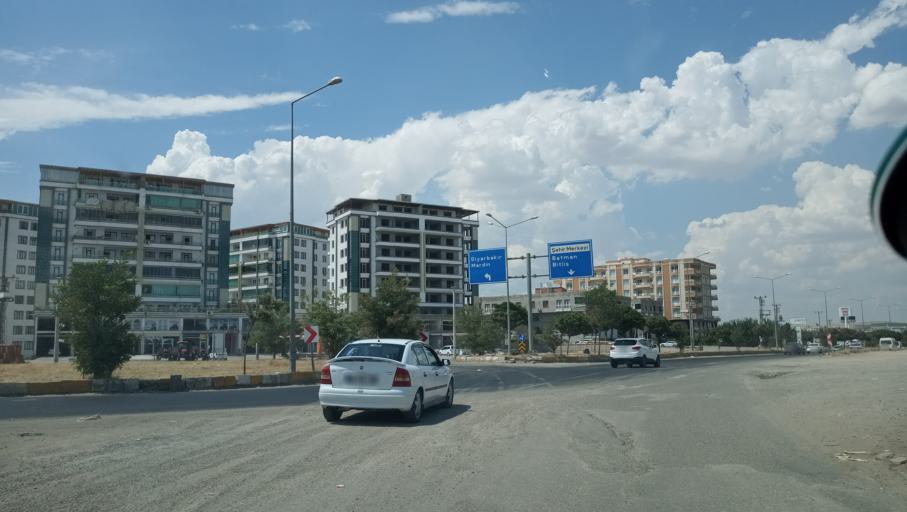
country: TR
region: Diyarbakir
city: Bismil
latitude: 37.8335
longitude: 40.6572
